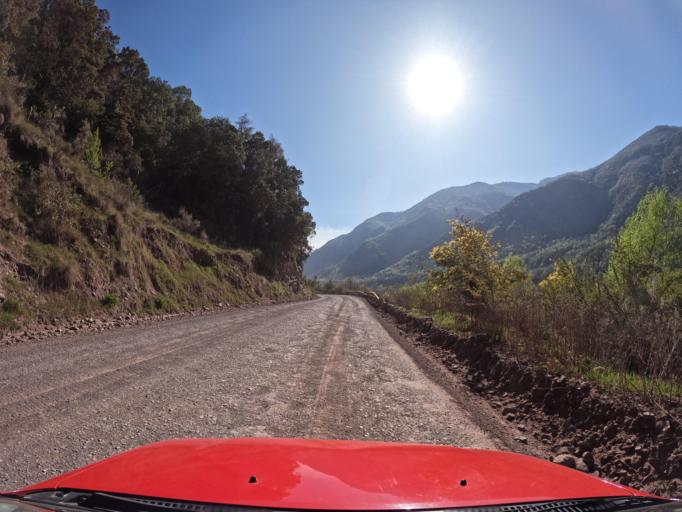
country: CL
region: O'Higgins
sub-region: Provincia de Colchagua
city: Chimbarongo
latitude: -35.0007
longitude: -70.7788
